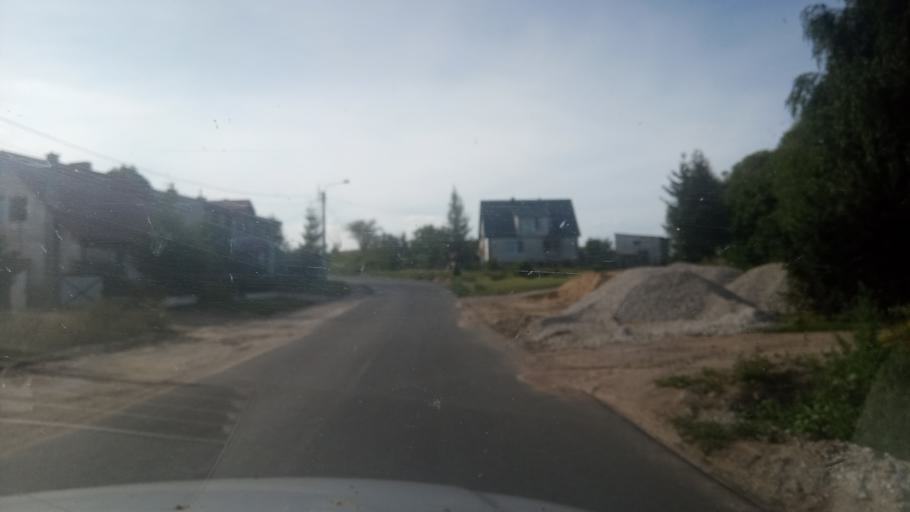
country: PL
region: Kujawsko-Pomorskie
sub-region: Powiat nakielski
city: Sadki
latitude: 53.1962
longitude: 17.3874
